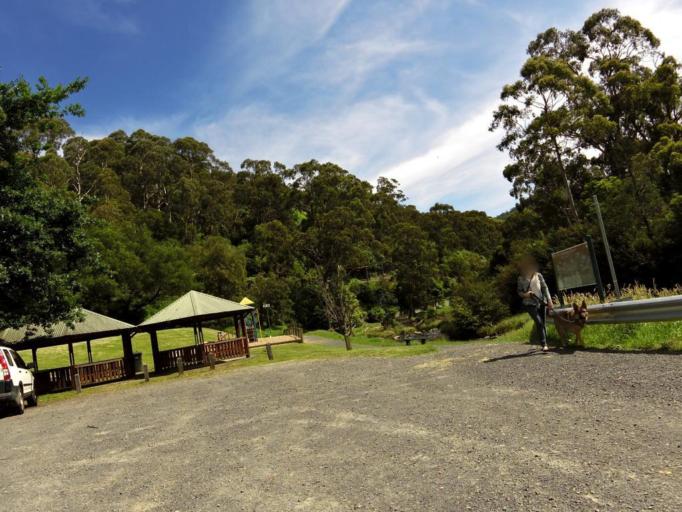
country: AU
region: Victoria
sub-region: Yarra Ranges
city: Millgrove
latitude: -37.7520
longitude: 145.6943
